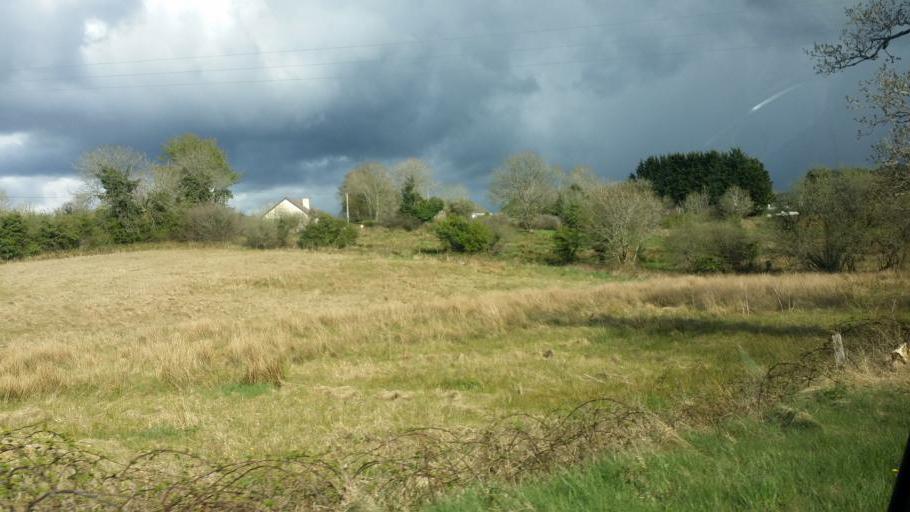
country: IE
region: Connaught
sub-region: County Leitrim
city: Manorhamilton
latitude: 54.3115
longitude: -8.1864
